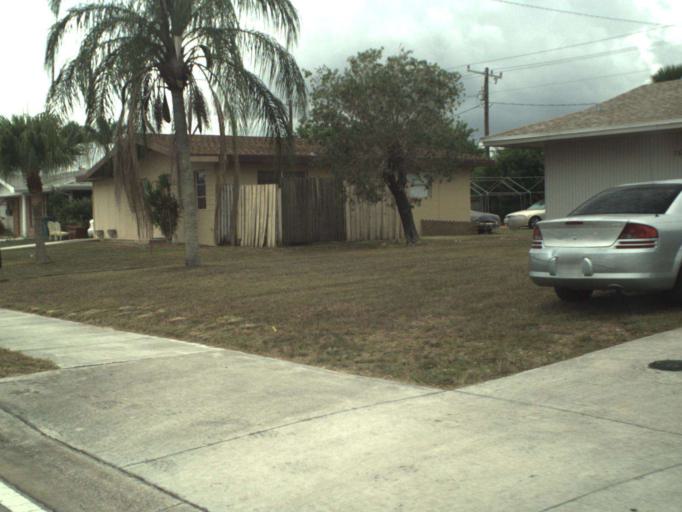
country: US
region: Florida
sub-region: Saint Lucie County
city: River Park
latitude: 27.3123
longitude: -80.3497
